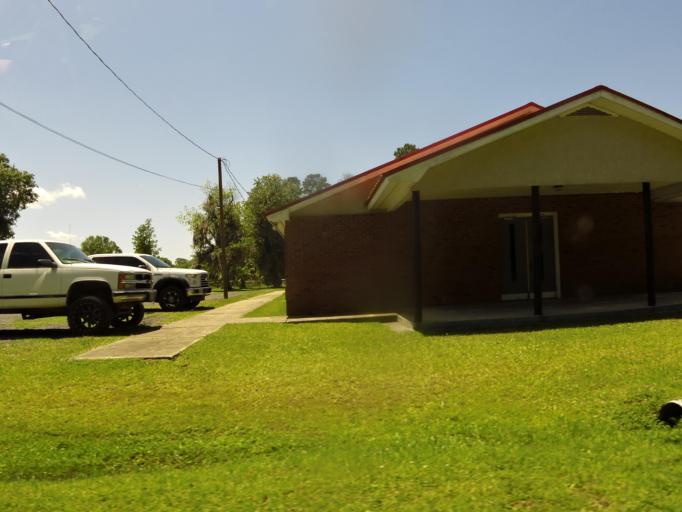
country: US
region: Florida
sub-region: Bradford County
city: Starke
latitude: 30.0479
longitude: -82.0748
